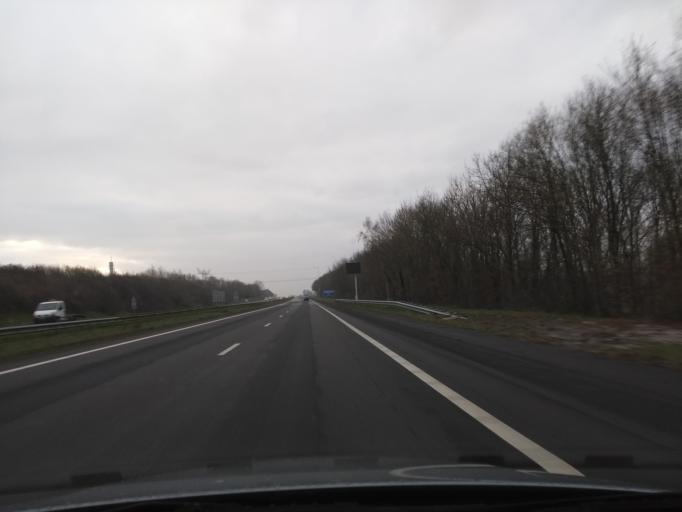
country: NL
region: Overijssel
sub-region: Gemeente Hengelo
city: Hengelo
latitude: 52.2556
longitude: 6.7527
